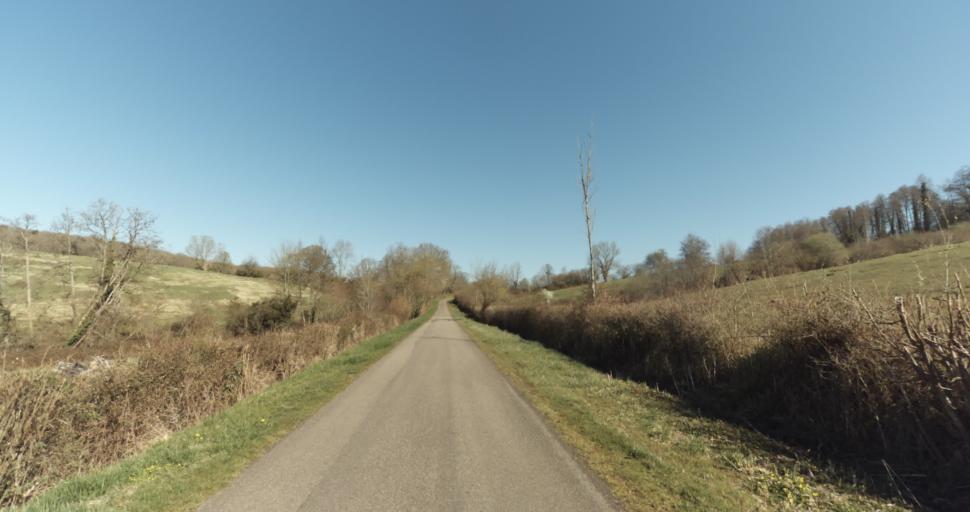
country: FR
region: Lower Normandy
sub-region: Departement du Calvados
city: Livarot
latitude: 48.9808
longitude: 0.0603
